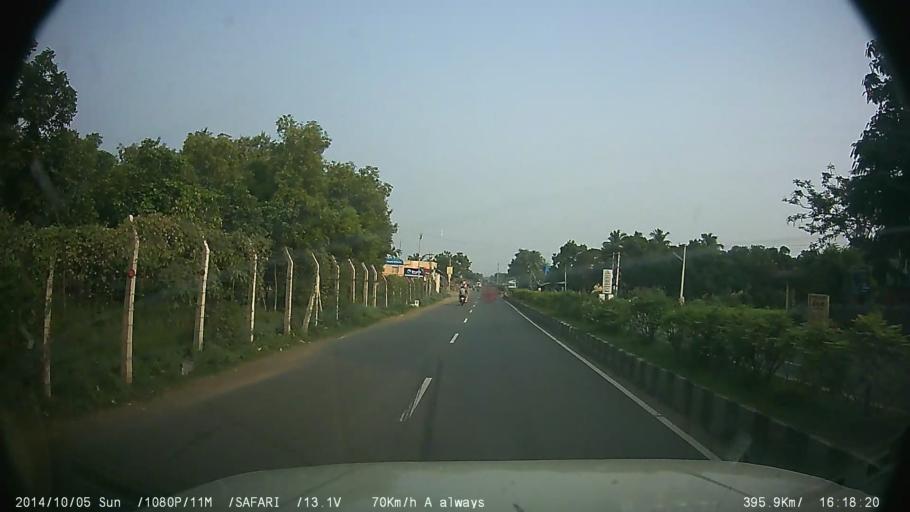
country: IN
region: Tamil Nadu
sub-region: Kancheepuram
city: Vengavasal
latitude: 12.8594
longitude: 80.1324
